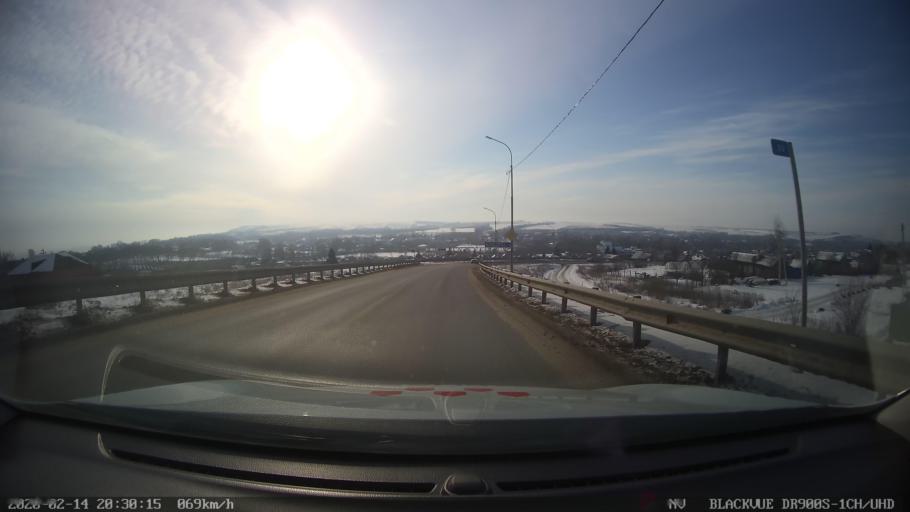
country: RU
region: Tatarstan
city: Stolbishchi
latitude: 55.4438
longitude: 48.9938
